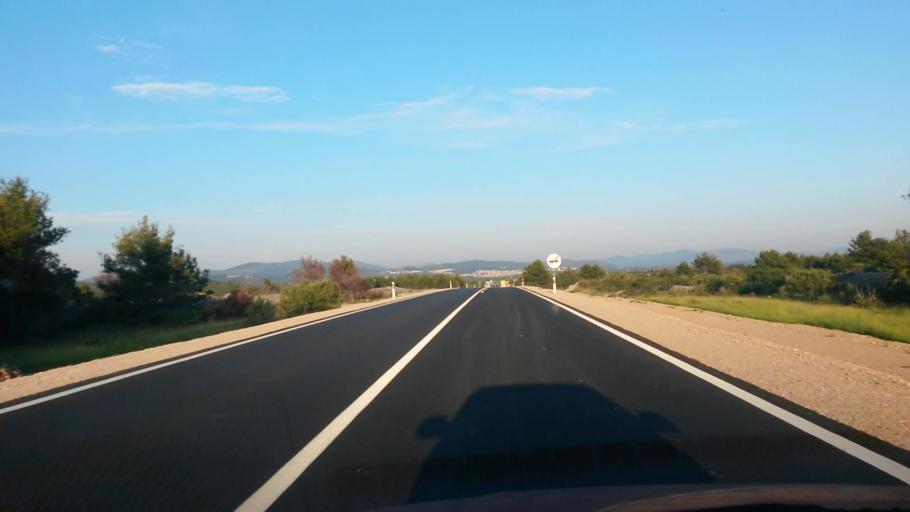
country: HR
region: Sibensko-Kniniska
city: Vodice
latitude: 43.7669
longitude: 15.8048
